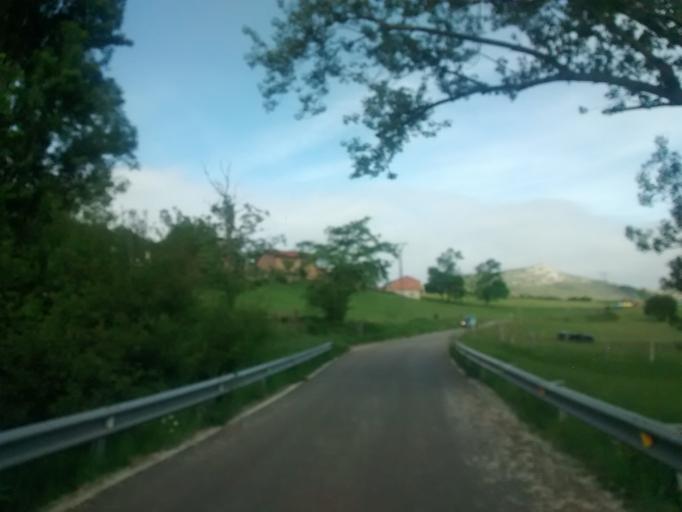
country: ES
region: Cantabria
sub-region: Provincia de Cantabria
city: Tresviso
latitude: 43.2430
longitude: -4.5640
